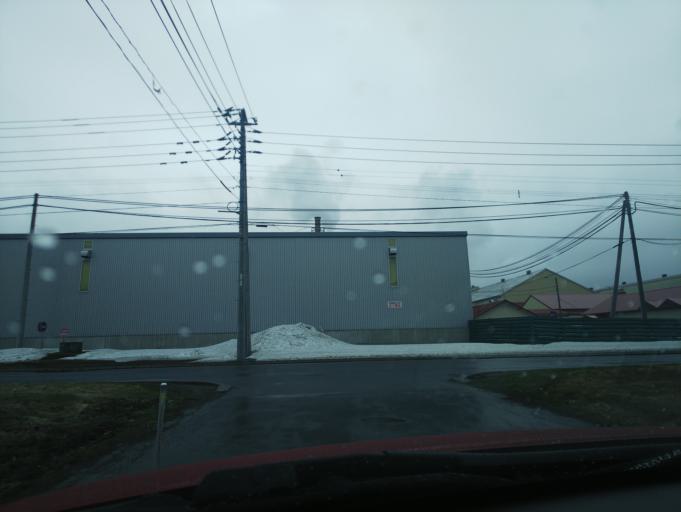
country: JP
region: Hokkaido
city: Nayoro
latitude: 44.3415
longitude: 142.4604
